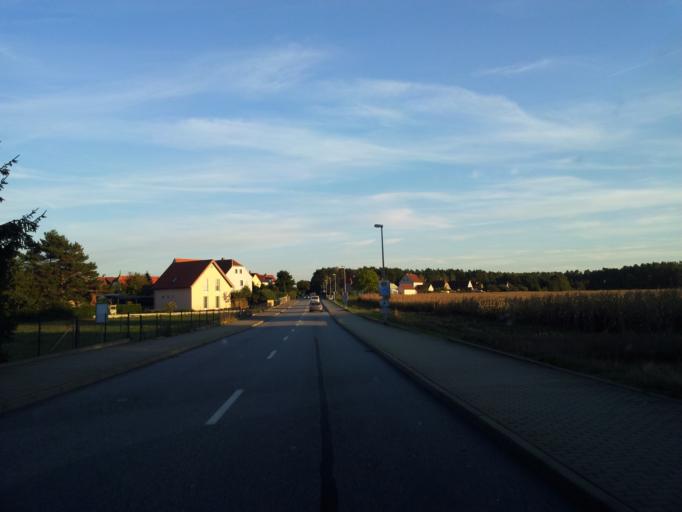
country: DE
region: Saxony
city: Ottendorf-Okrilla
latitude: 51.1814
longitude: 13.8476
